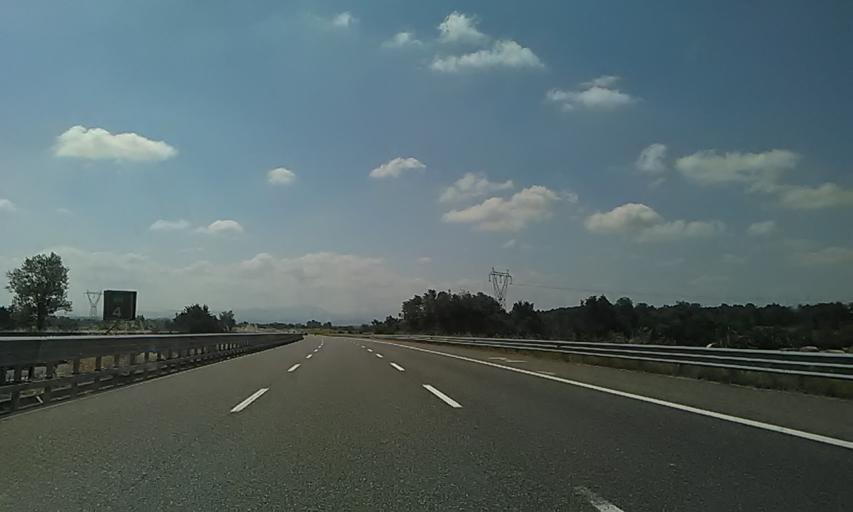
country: IT
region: Piedmont
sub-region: Provincia di Alessandria
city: Predosa
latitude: 44.7697
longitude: 8.6311
